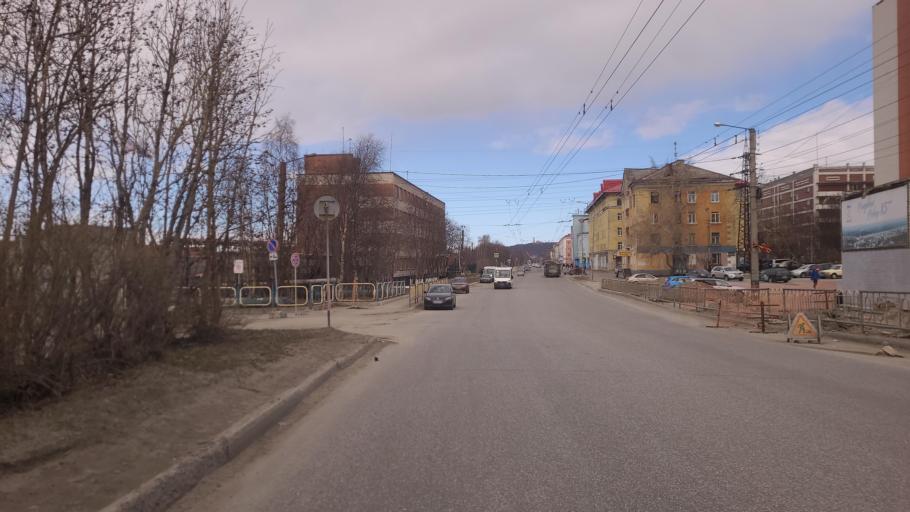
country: RU
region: Murmansk
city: Murmansk
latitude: 68.9577
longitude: 33.0628
